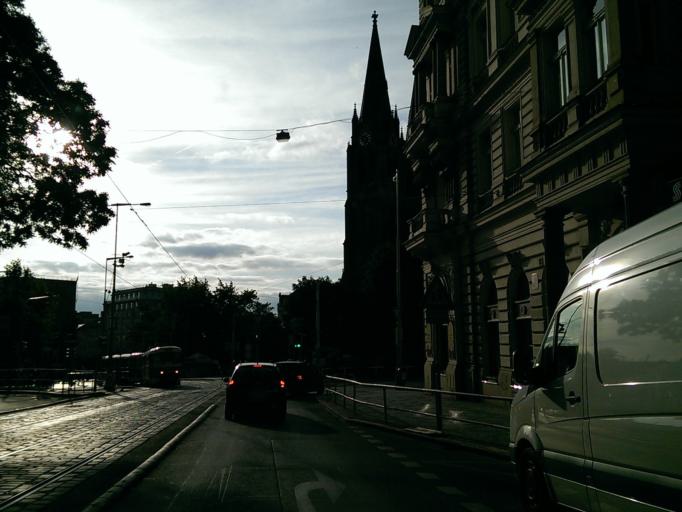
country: CZ
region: Praha
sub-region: Praha 8
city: Karlin
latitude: 50.0747
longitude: 14.4380
